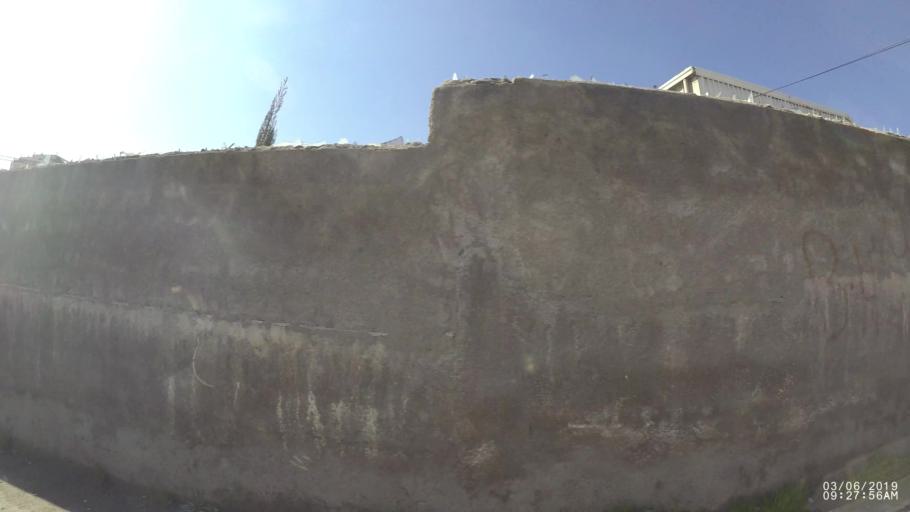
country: JO
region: Zarqa
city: Russeifa
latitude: 31.9932
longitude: 35.9923
